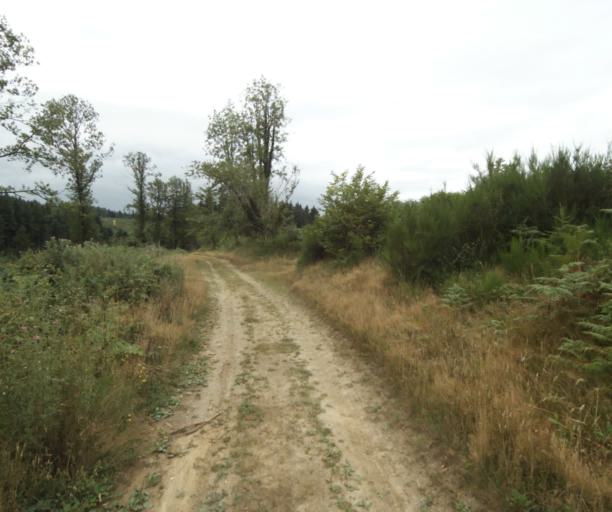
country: FR
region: Midi-Pyrenees
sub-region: Departement du Tarn
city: Soreze
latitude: 43.4208
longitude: 2.1216
